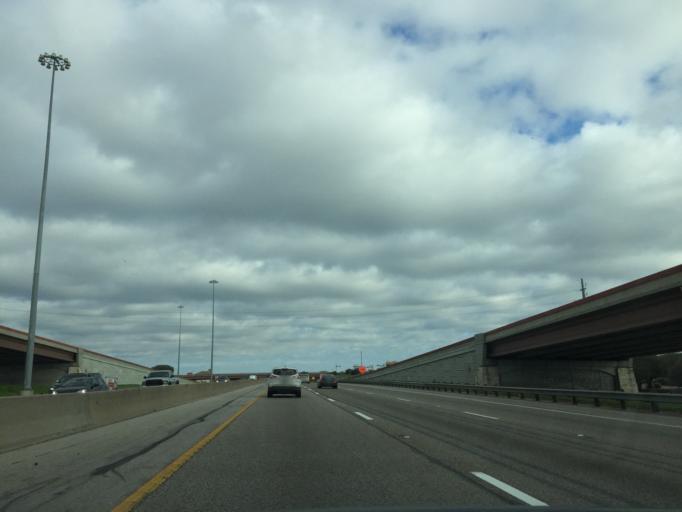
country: US
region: Texas
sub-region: Williamson County
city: Round Rock
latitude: 30.4849
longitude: -97.6753
